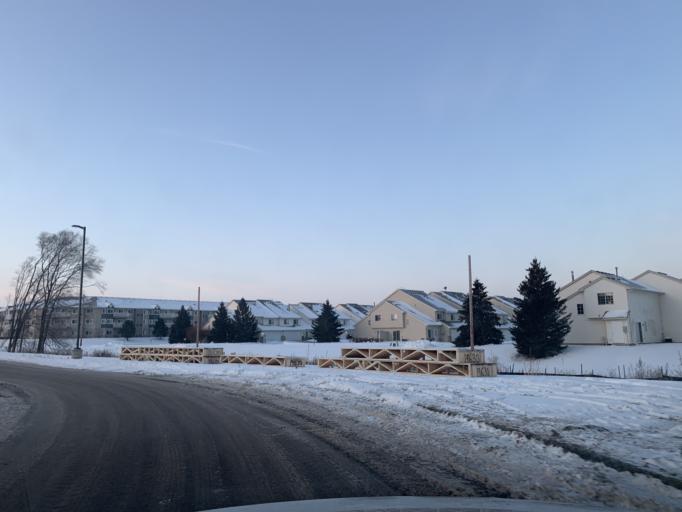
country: US
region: Minnesota
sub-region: Scott County
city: Shakopee
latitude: 44.7914
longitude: -93.4897
